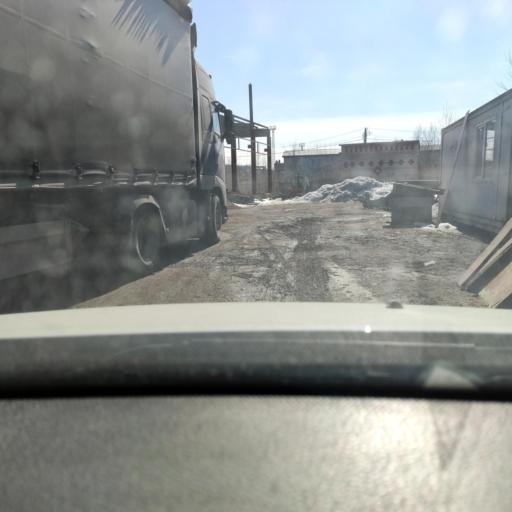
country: RU
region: Bashkortostan
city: Ufa
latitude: 54.7480
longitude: 55.9247
